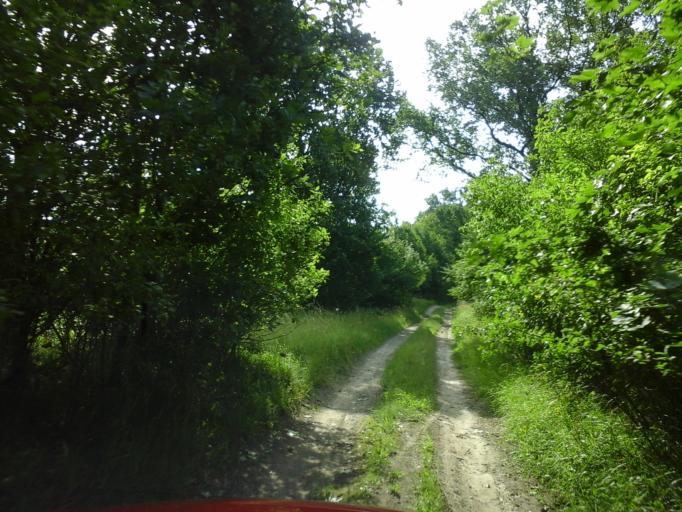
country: PL
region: West Pomeranian Voivodeship
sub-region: Powiat choszczenski
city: Krzecin
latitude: 53.1181
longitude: 15.5236
